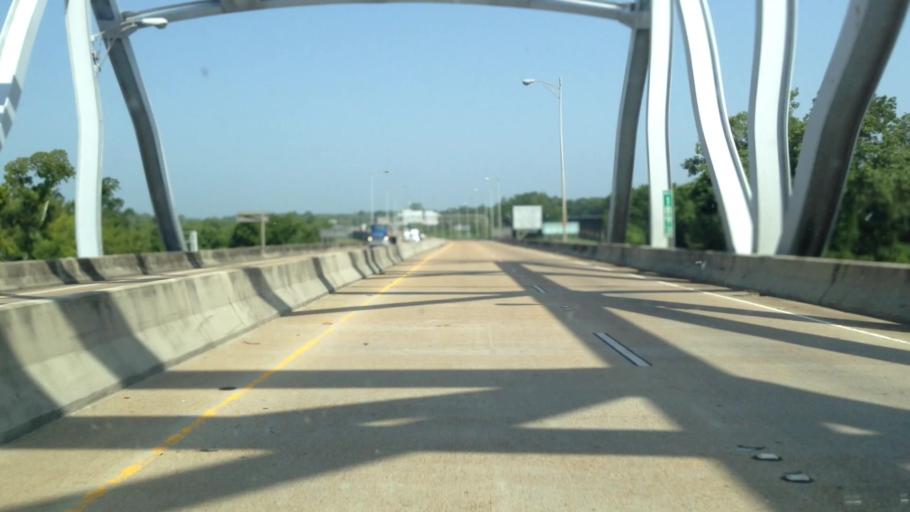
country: US
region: Mississippi
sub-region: Warren County
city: Vicksburg
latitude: 32.3163
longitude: -90.9106
